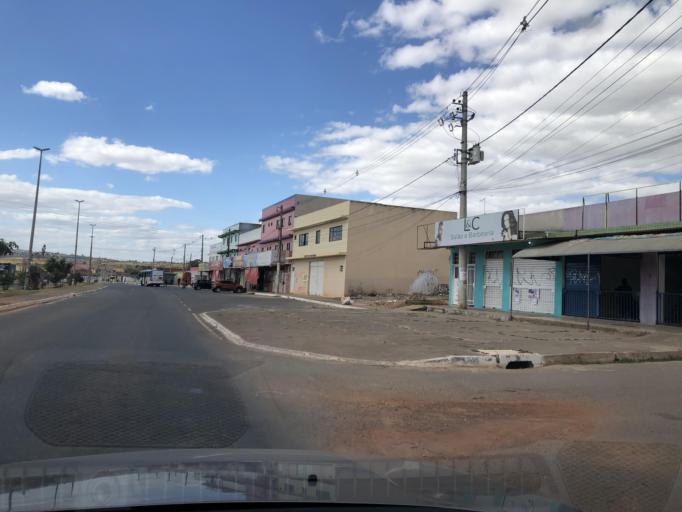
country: BR
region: Federal District
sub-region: Brasilia
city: Brasilia
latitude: -15.8866
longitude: -48.1467
